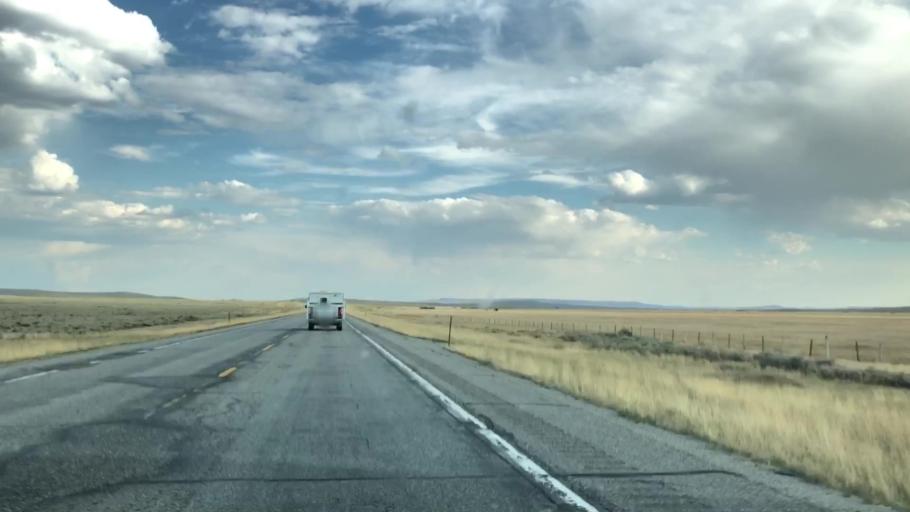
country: US
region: Wyoming
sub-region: Sublette County
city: Pinedale
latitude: 43.0433
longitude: -110.1431
